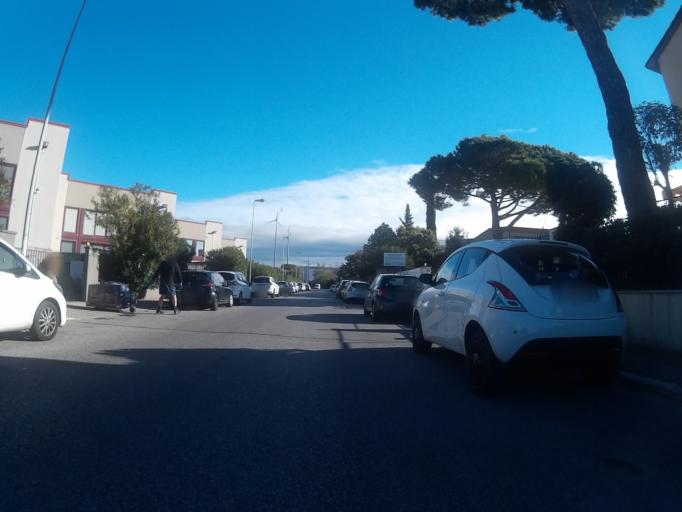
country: IT
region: Tuscany
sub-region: Provincia di Livorno
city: Livorno
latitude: 43.5668
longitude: 10.3363
